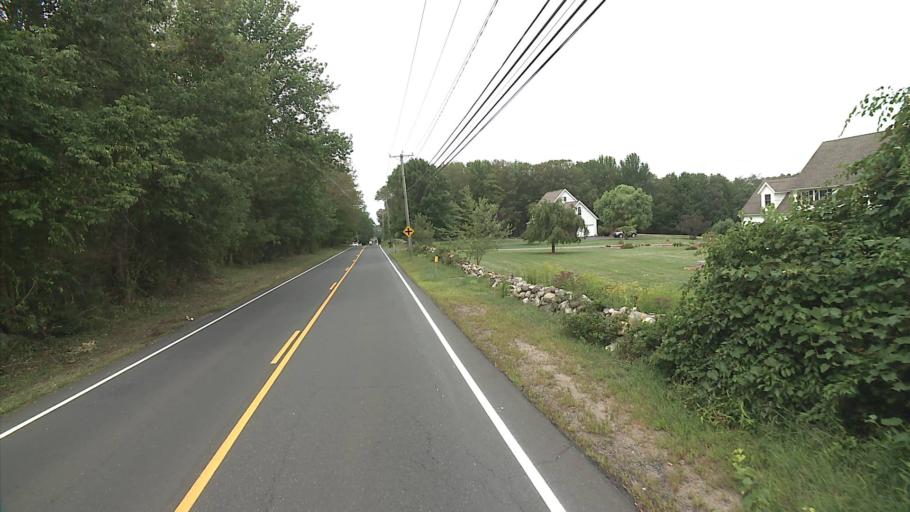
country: US
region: Connecticut
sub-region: New London County
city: Colchester
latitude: 41.5544
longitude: -72.3141
